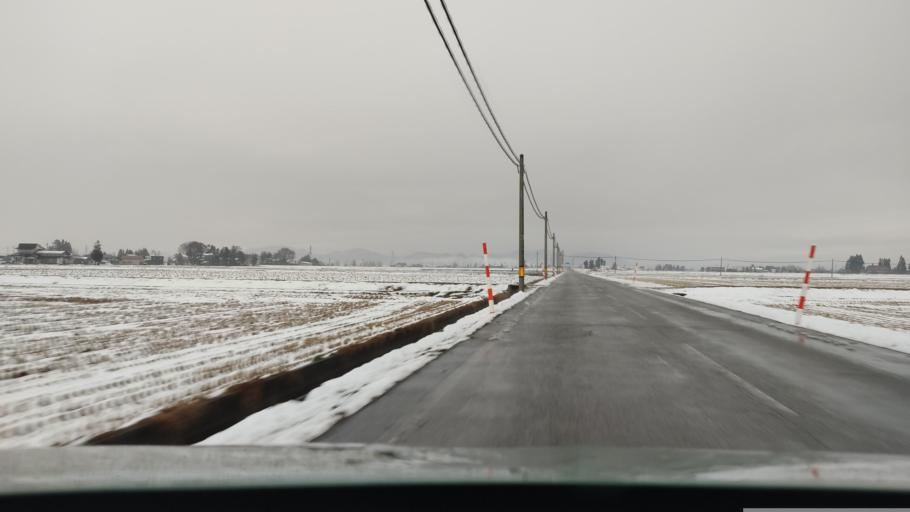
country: JP
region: Akita
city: Omagari
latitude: 39.4755
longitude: 140.5290
